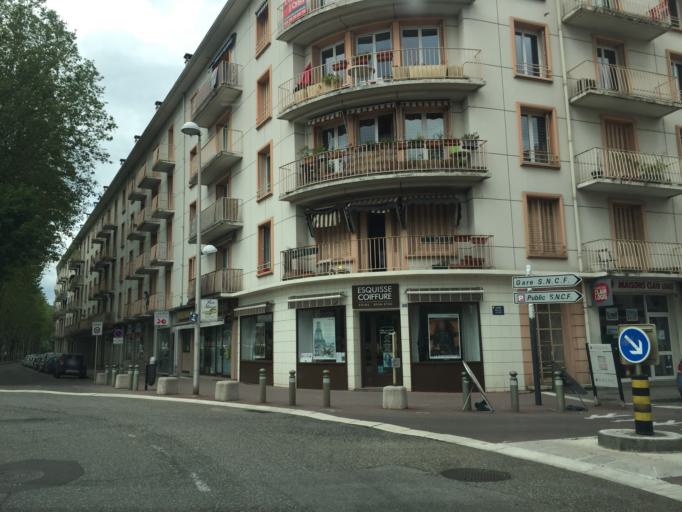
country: FR
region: Rhone-Alpes
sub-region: Departement de la Savoie
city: Chambery
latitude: 45.5706
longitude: 5.9180
